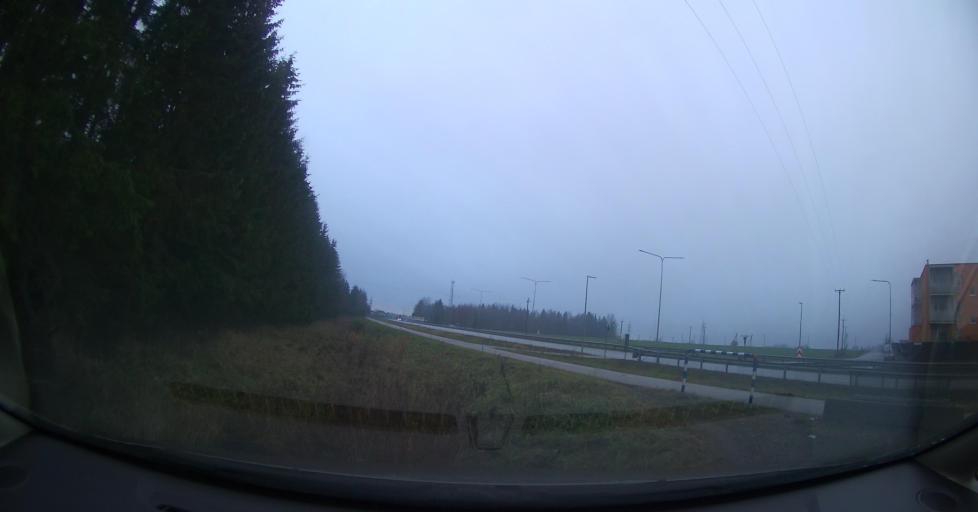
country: EE
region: Tartu
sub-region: Tartu linn
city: Tartu
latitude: 58.3727
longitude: 26.7919
